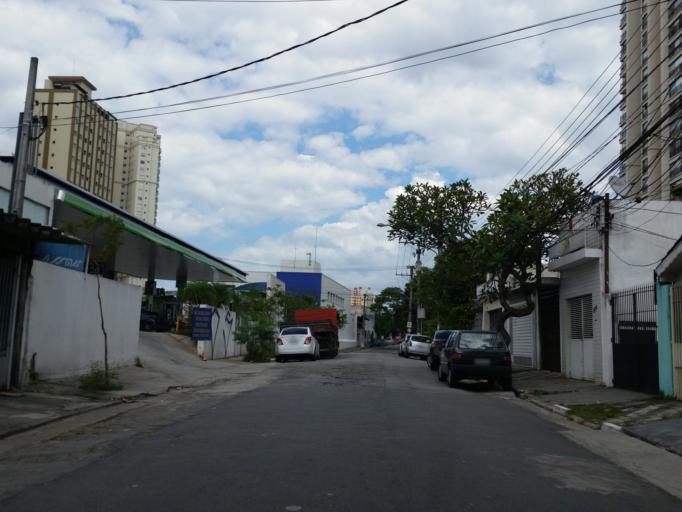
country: BR
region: Sao Paulo
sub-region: Diadema
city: Diadema
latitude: -23.6506
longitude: -46.6702
